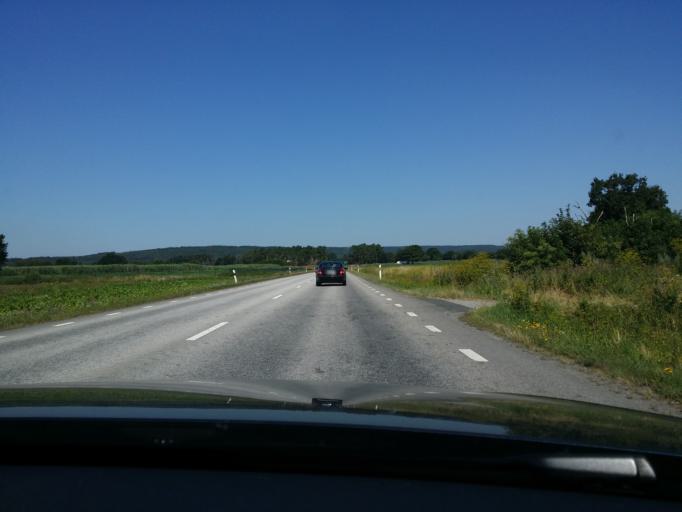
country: SE
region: Blekinge
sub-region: Solvesborgs Kommun
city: Soelvesborg
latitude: 56.0564
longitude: 14.6360
